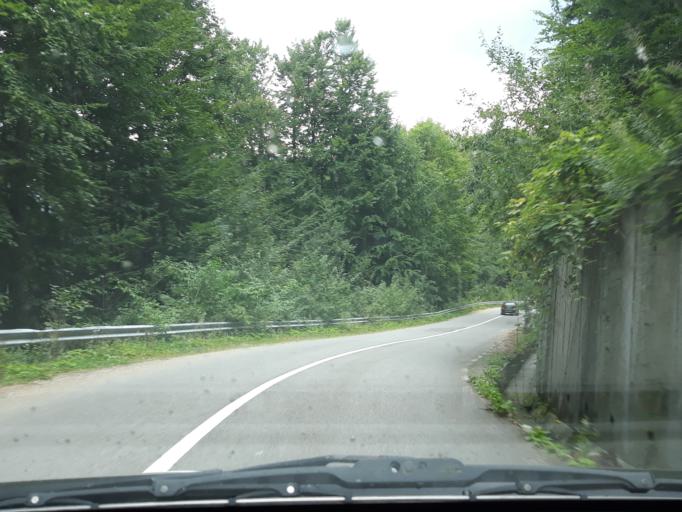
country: RO
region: Bihor
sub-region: Comuna Pietroasa
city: Pietroasa
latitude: 46.5952
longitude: 22.6710
